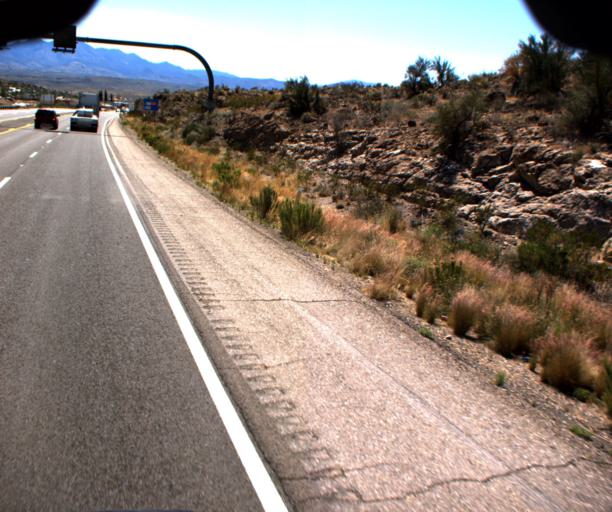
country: US
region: Arizona
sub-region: Mohave County
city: Kingman
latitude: 35.1999
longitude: -114.0795
